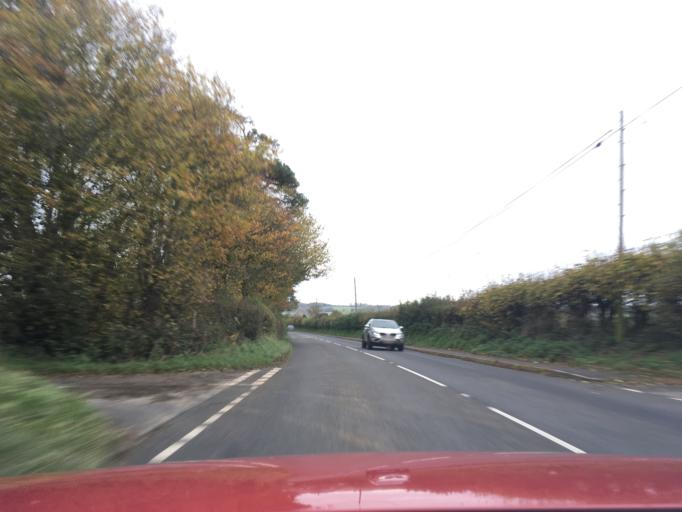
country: GB
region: England
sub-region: Dorset
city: Sherborne
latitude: 50.9562
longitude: -2.5359
